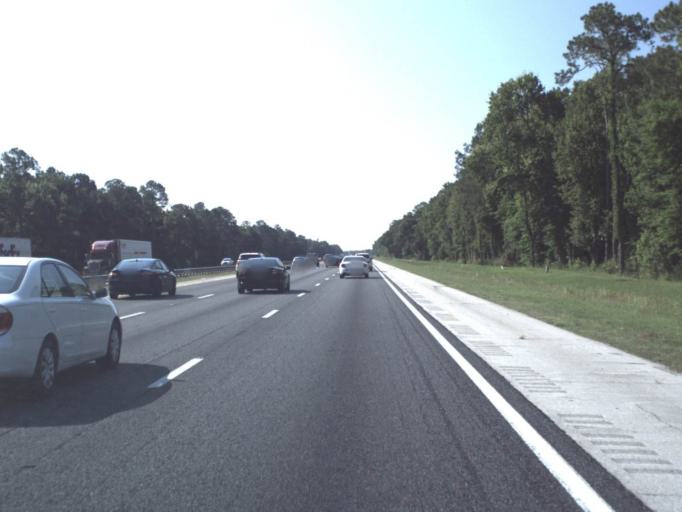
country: US
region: Florida
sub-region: Saint Johns County
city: Saint Augustine
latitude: 29.9447
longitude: -81.4340
